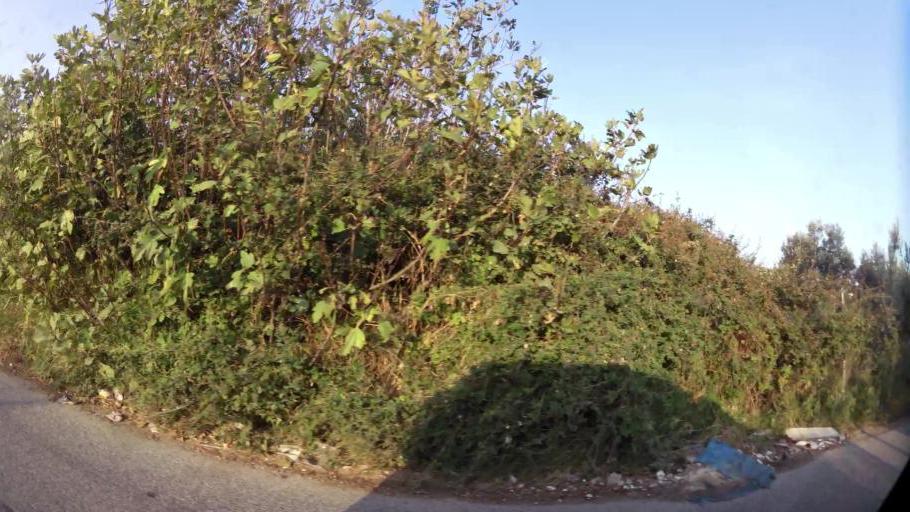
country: GR
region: Attica
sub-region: Nomarchia Athinas
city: Kamateron
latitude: 38.0549
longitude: 23.7144
